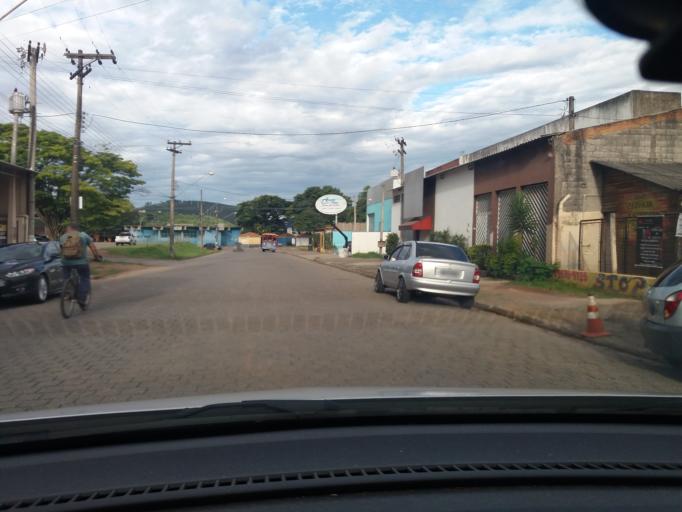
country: BR
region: Sao Paulo
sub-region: Bom Jesus Dos Perdoes
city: Bom Jesus dos Perdoes
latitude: -23.1316
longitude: -46.4679
